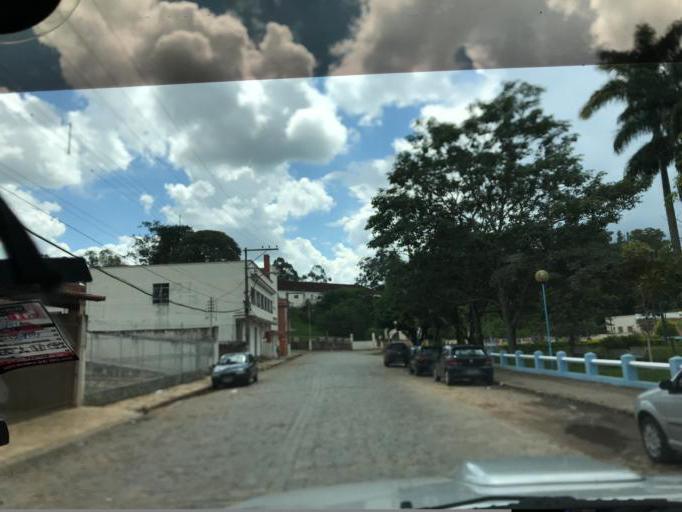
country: BR
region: Minas Gerais
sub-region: Cambuquira
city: Cambuquira
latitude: -21.8494
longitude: -45.2967
